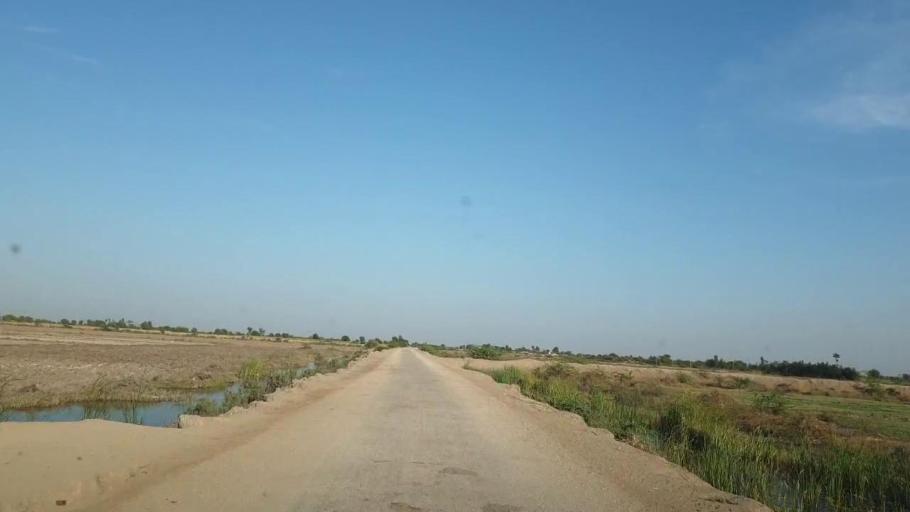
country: PK
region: Sindh
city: Kunri
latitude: 25.0911
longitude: 69.4151
